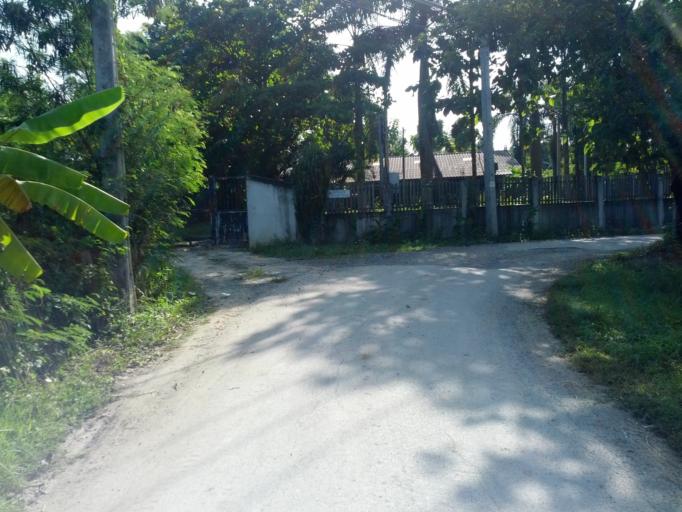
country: TH
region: Chiang Mai
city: San Kamphaeng
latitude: 18.7706
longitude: 99.1184
